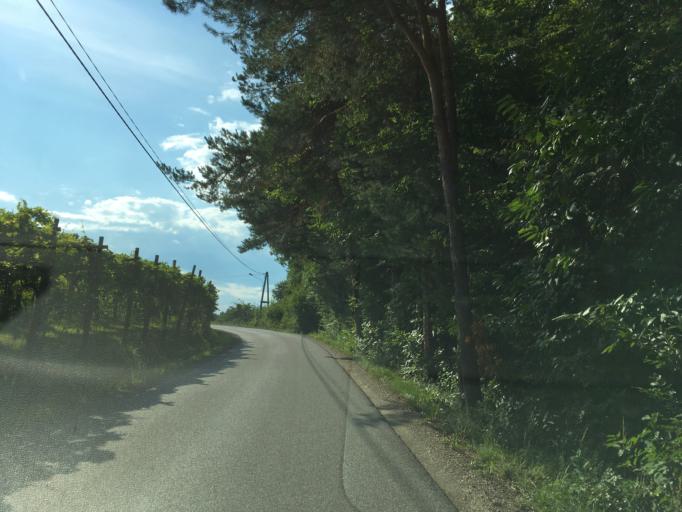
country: AT
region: Styria
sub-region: Politischer Bezirk Leibnitz
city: Sankt Nikolai im Sausal
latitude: 46.8057
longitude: 15.4538
